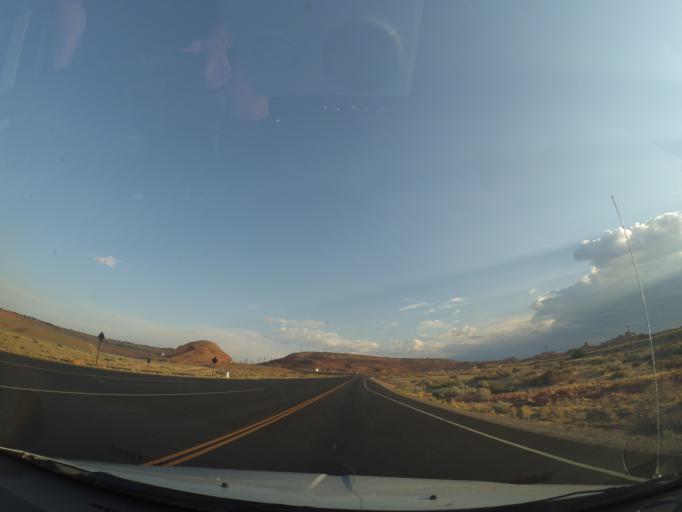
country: US
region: Arizona
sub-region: Coconino County
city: Page
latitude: 36.9426
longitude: -111.4935
